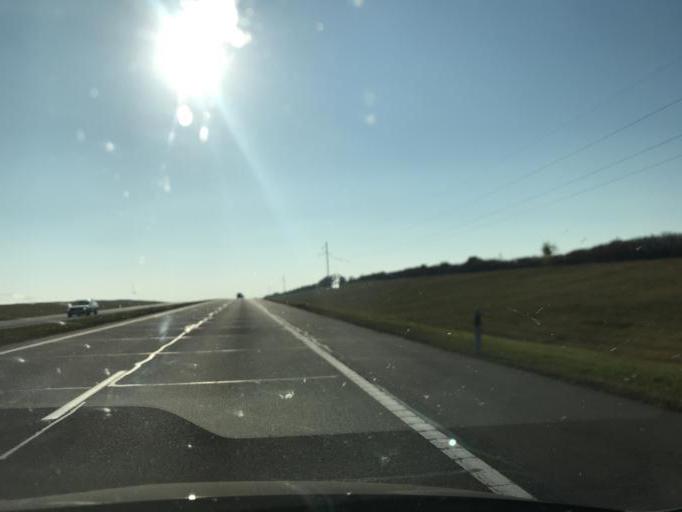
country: BY
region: Minsk
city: Novy Svyerzhan'
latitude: 53.4708
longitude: 26.6183
